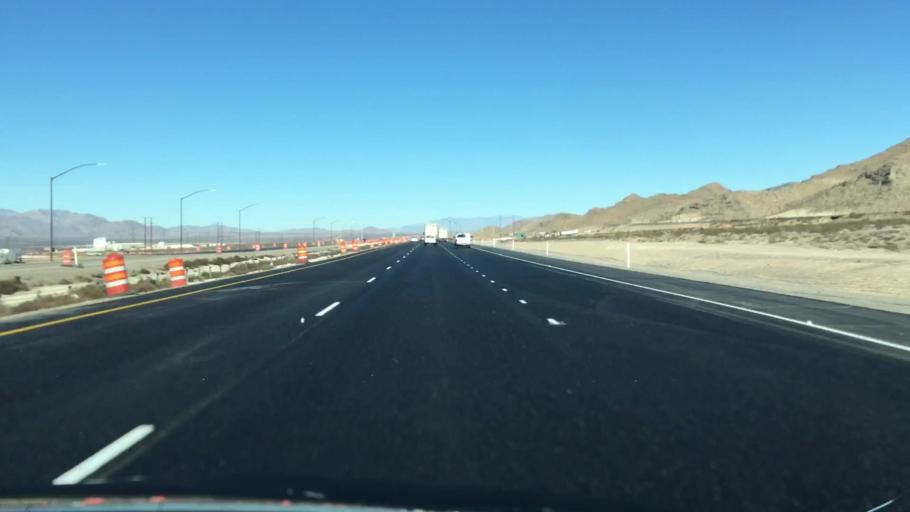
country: US
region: Nevada
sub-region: Clark County
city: Nellis Air Force Base
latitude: 36.3739
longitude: -114.8957
